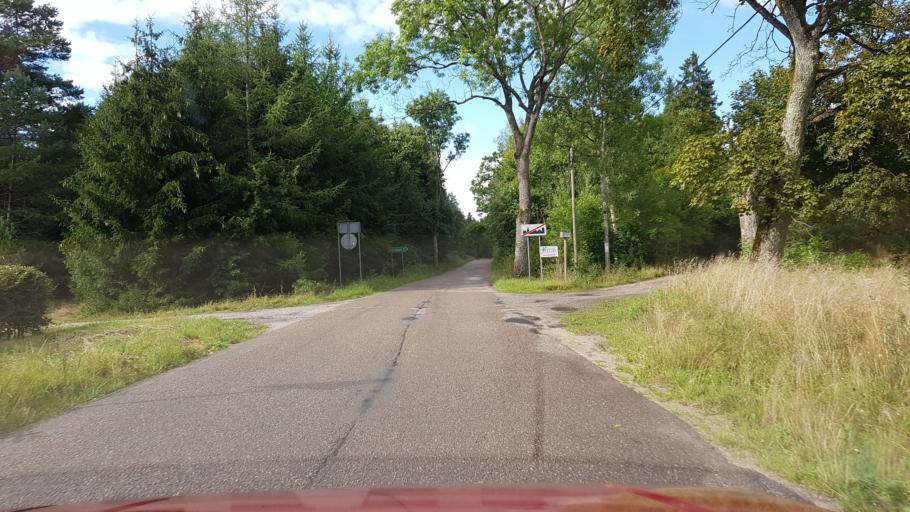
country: PL
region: West Pomeranian Voivodeship
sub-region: Powiat bialogardzki
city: Tychowo
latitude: 54.0167
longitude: 16.3941
